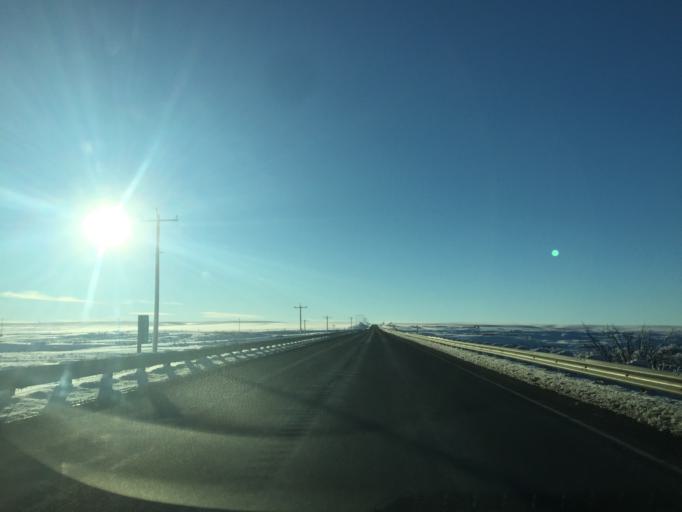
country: US
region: Washington
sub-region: Okanogan County
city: Coulee Dam
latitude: 47.7402
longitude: -118.8405
